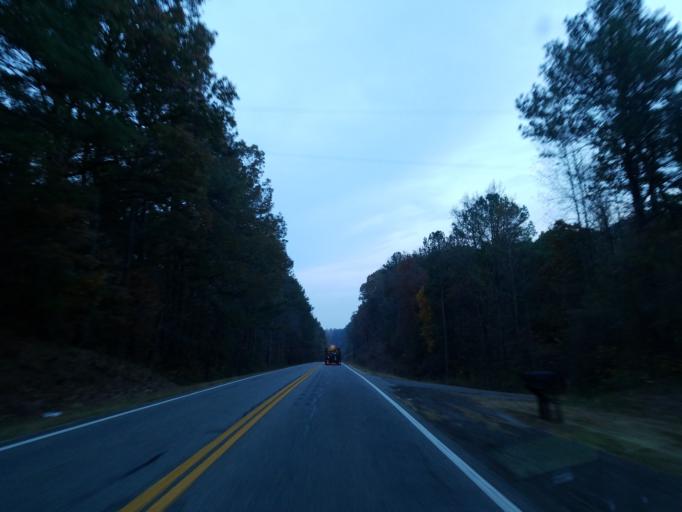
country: US
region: Georgia
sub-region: Pickens County
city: Jasper
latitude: 34.5230
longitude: -84.5710
